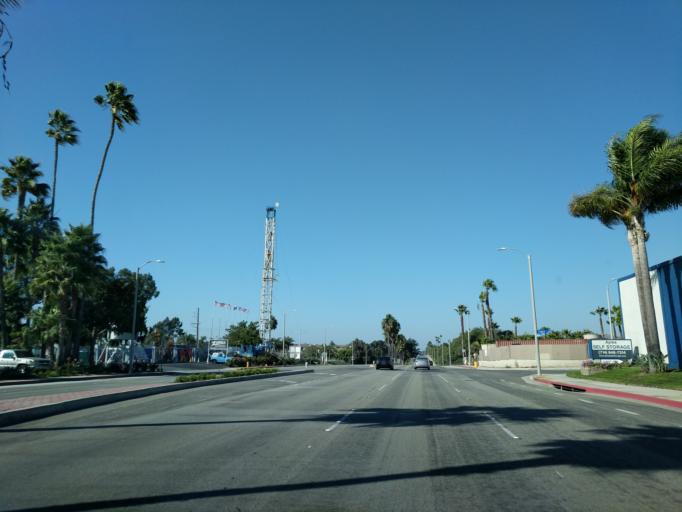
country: US
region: California
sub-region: Orange County
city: Huntington Beach
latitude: 33.6889
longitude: -118.0061
